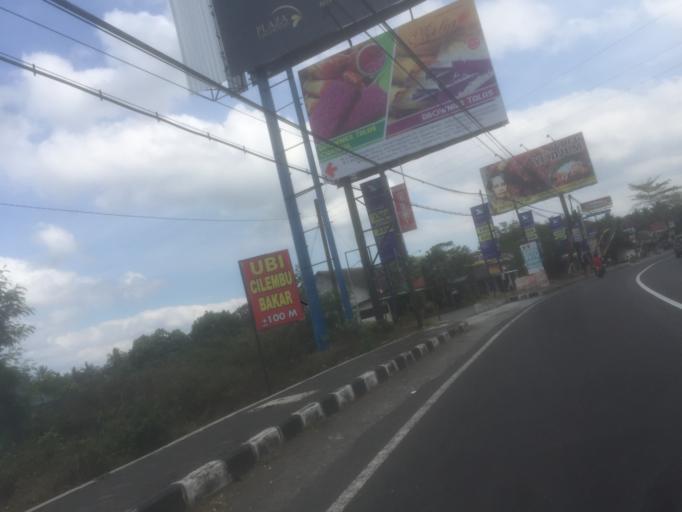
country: ID
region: Daerah Istimewa Yogyakarta
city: Sleman
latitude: -7.6578
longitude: 110.3264
